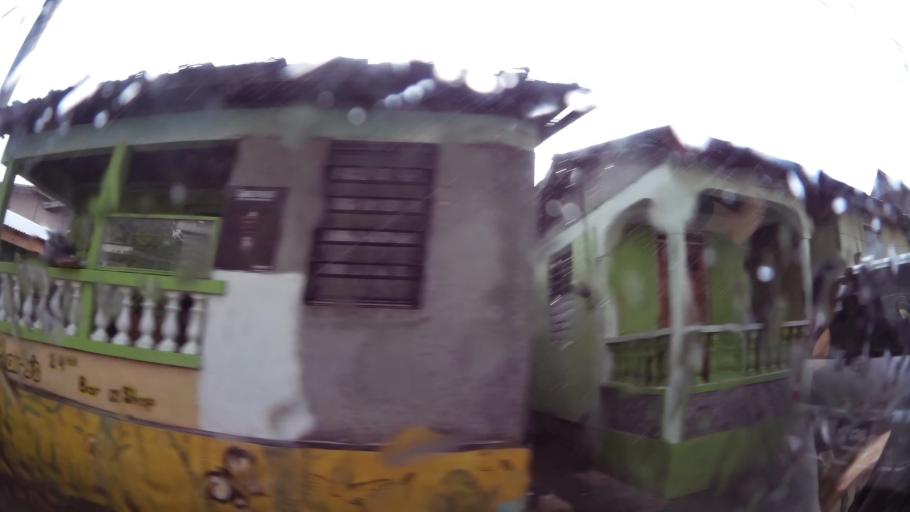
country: DM
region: Saint Paul
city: Mahaut
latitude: 15.3618
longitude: -61.3974
